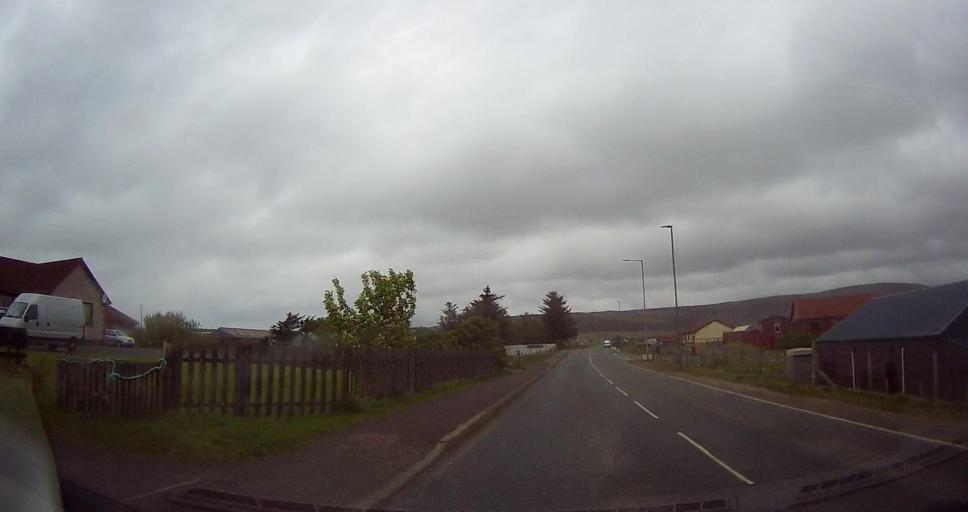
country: GB
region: Scotland
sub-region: Shetland Islands
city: Lerwick
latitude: 60.3928
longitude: -1.3660
